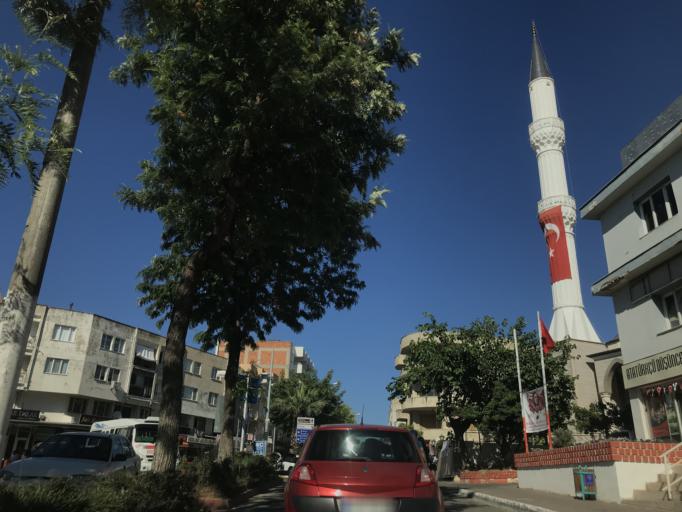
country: TR
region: Aydin
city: Davutlar
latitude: 37.7334
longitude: 27.2940
